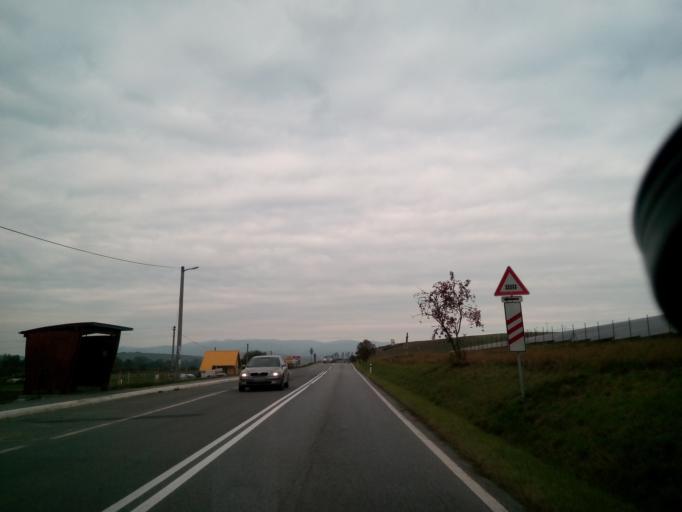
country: SK
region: Presovsky
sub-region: Okres Presov
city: Presov
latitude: 49.0682
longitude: 21.3367
